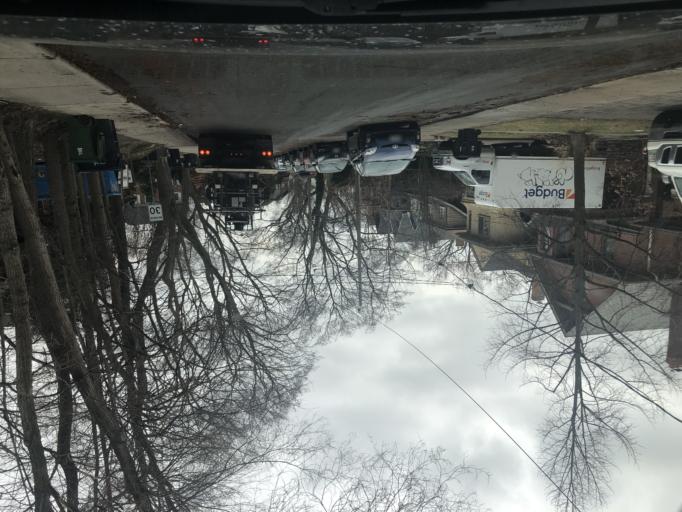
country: CA
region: Ontario
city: Toronto
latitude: 43.6788
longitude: -79.3539
